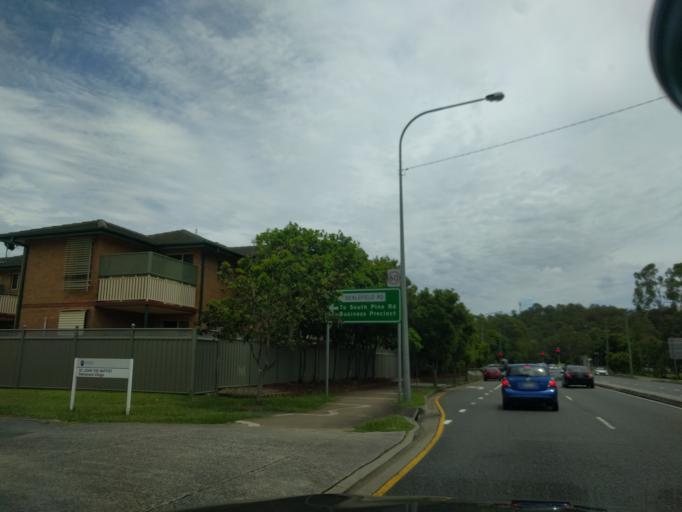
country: AU
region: Queensland
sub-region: Brisbane
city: Stafford
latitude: -27.4194
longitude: 152.9996
